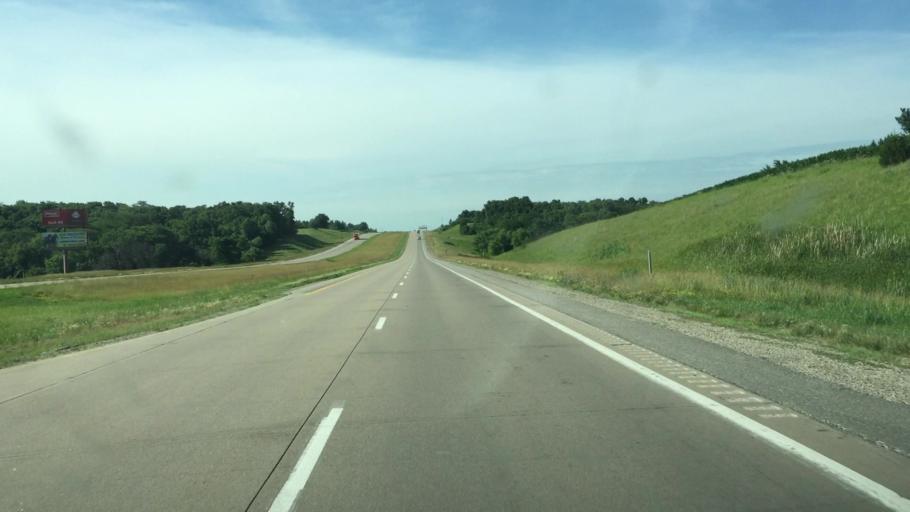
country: US
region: Iowa
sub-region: Henry County
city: Winfield
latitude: 41.2065
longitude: -91.5291
